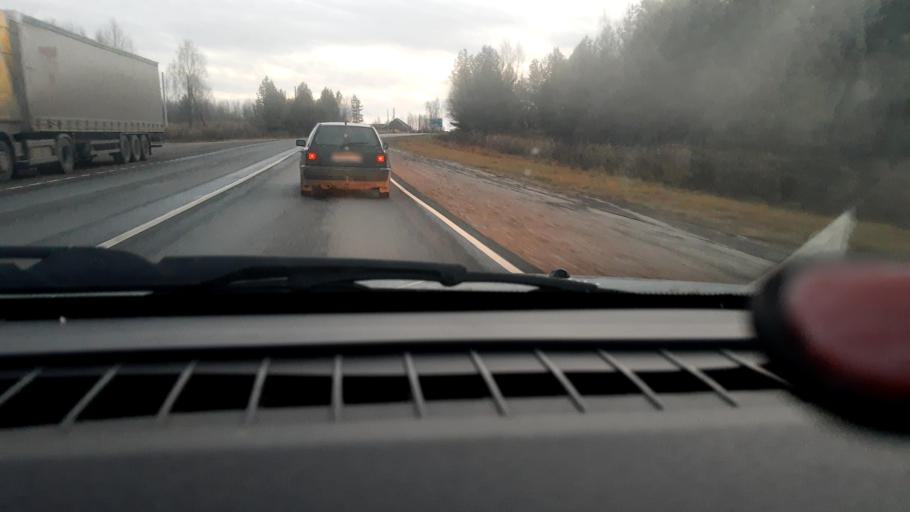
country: RU
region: Nizjnij Novgorod
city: Krasnyye Baki
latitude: 57.0166
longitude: 45.1164
